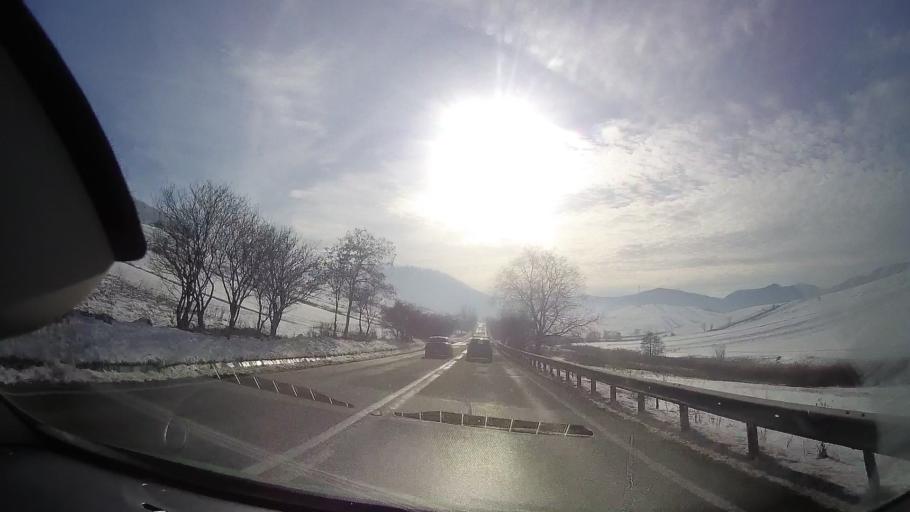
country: RO
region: Neamt
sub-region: Comuna Garcina
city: Garcina
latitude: 46.9882
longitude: 26.3607
